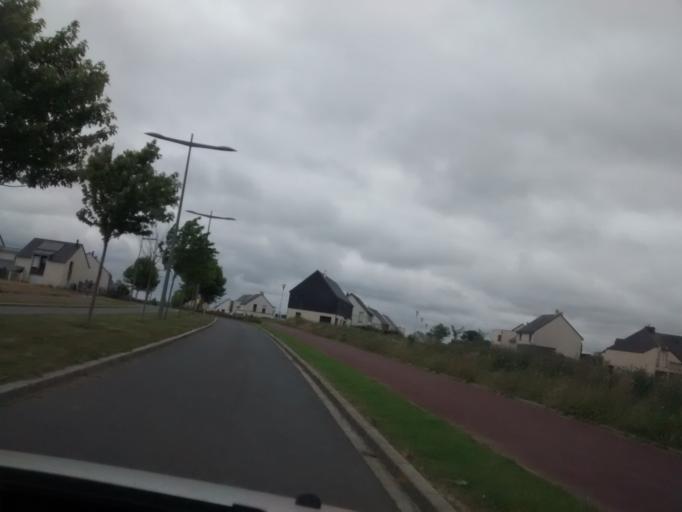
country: FR
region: Brittany
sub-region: Departement d'Ille-et-Vilaine
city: Saint-Gregoire
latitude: 48.1588
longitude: -1.6750
